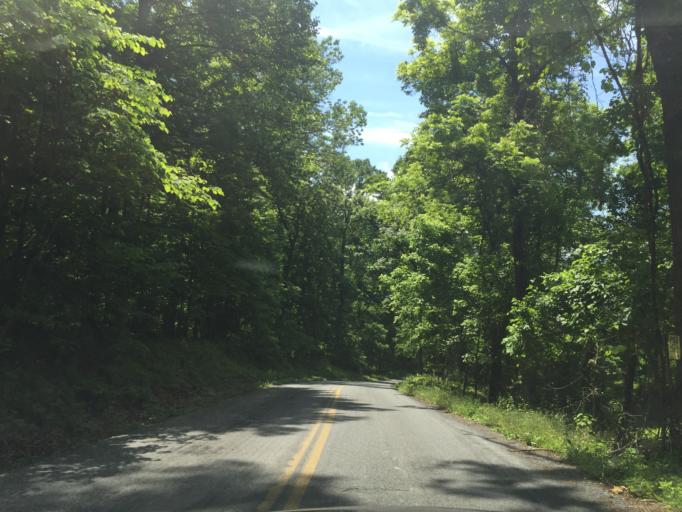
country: US
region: Virginia
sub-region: Warren County
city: Apple Mountain Lake
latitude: 38.9658
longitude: -78.1224
